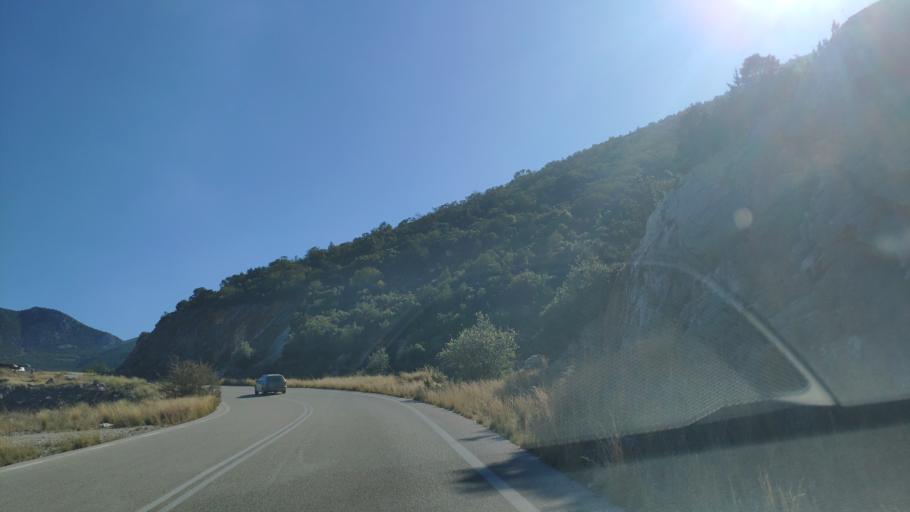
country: GR
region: Peloponnese
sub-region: Nomos Argolidos
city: Palaia Epidavros
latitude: 37.6169
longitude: 23.1493
